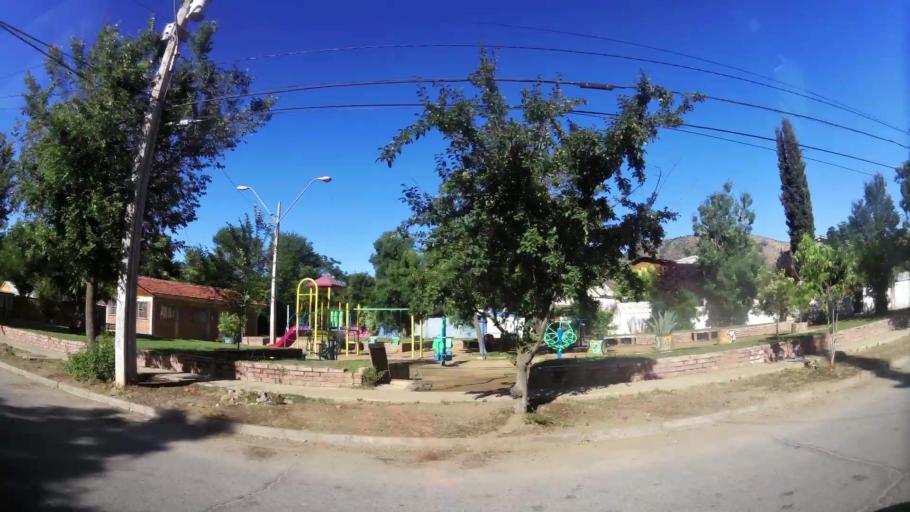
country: CL
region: Santiago Metropolitan
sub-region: Provincia de Chacabuco
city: Lampa
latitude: -33.3993
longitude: -71.1211
